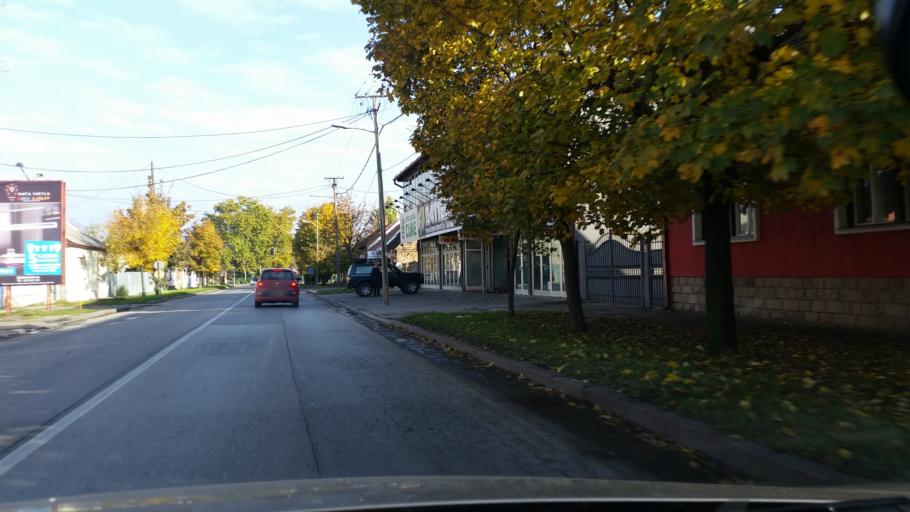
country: RS
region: Autonomna Pokrajina Vojvodina
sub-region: Srednjebanatski Okrug
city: Zrenjanin
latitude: 45.3773
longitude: 20.4062
